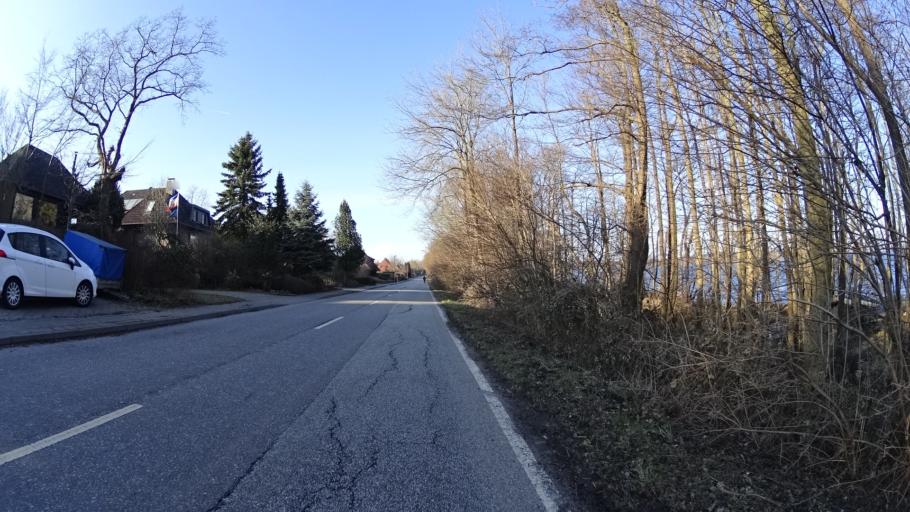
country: DE
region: Schleswig-Holstein
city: Martensrade
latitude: 54.3132
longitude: 10.3824
